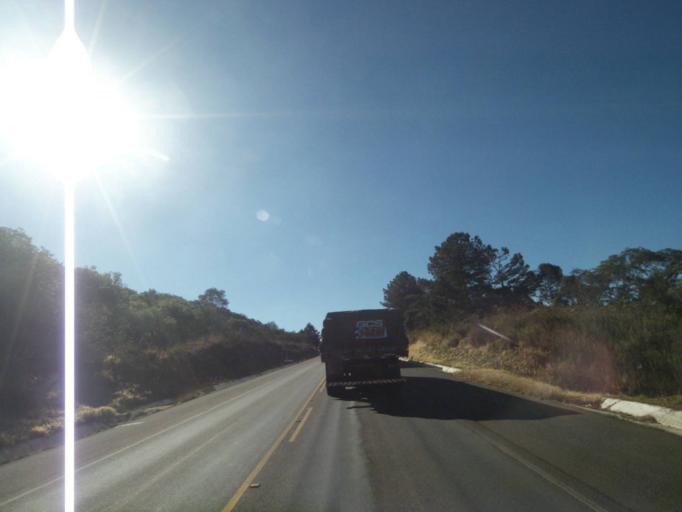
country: BR
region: Parana
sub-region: Tibagi
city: Tibagi
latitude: -24.6498
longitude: -50.4531
